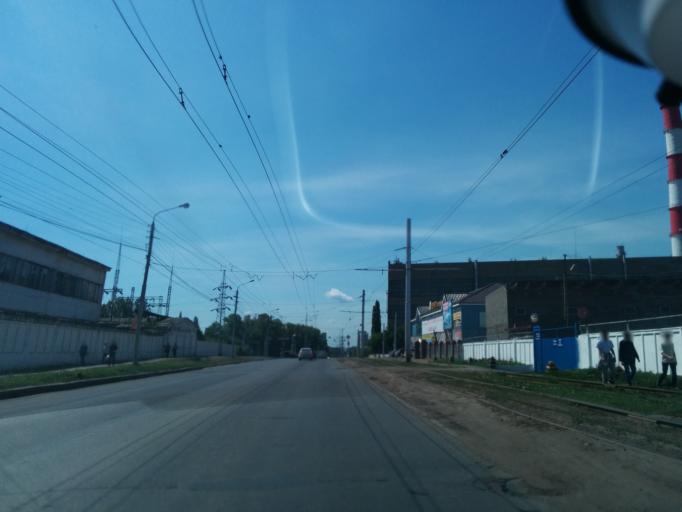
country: RU
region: Bashkortostan
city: Ufa
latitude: 54.7426
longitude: 55.9756
